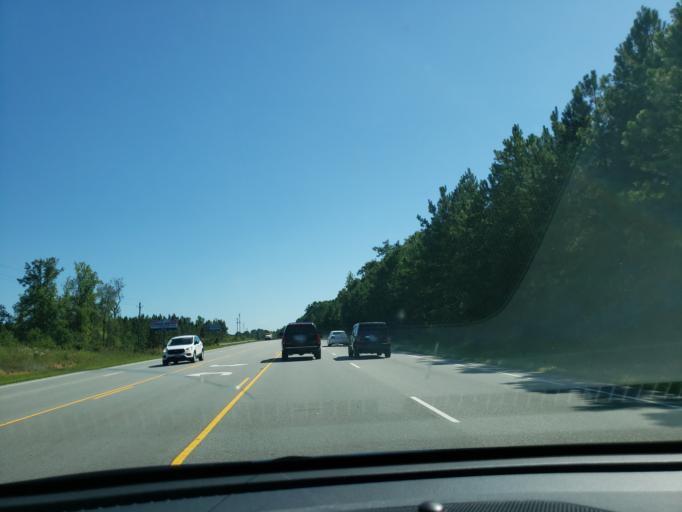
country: US
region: North Carolina
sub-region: Lee County
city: Broadway
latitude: 35.3576
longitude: -79.1097
